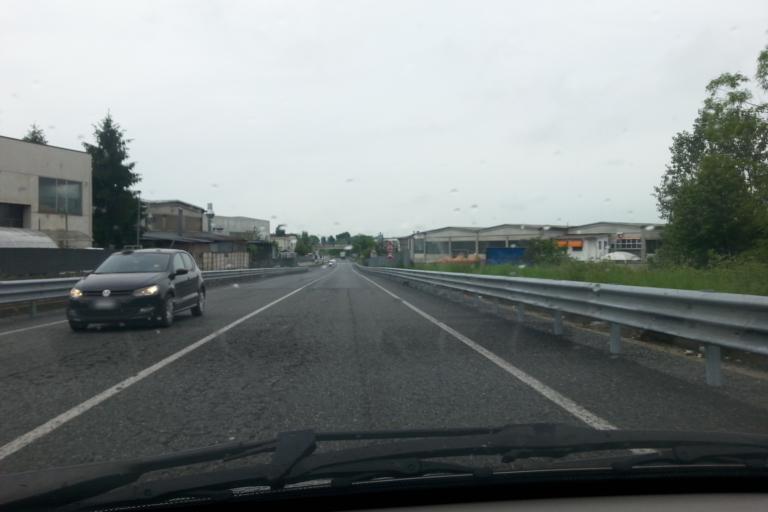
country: IT
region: Piedmont
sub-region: Provincia di Torino
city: Alpignano
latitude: 45.1099
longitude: 7.5074
